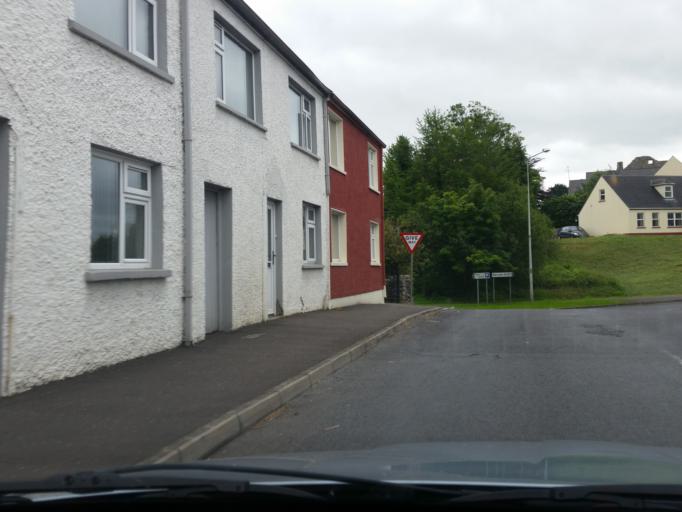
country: GB
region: Northern Ireland
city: Lisnaskea
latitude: 54.2520
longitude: -7.4453
